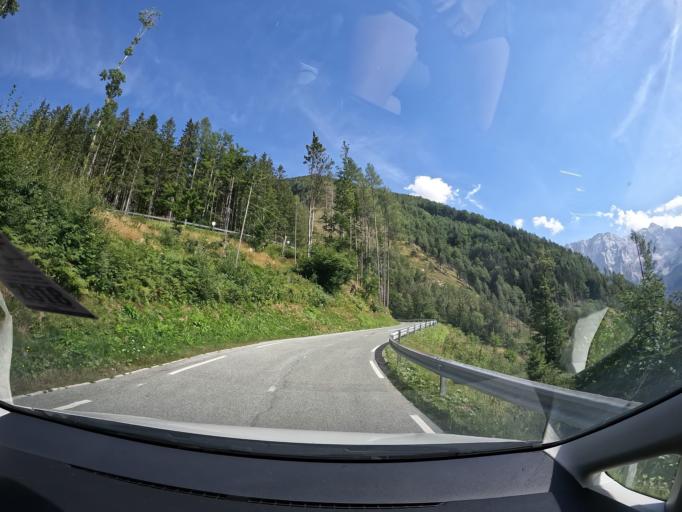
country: AT
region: Carinthia
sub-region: Politischer Bezirk Sankt Veit an der Glan
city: Liebenfels
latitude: 46.7069
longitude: 14.2829
